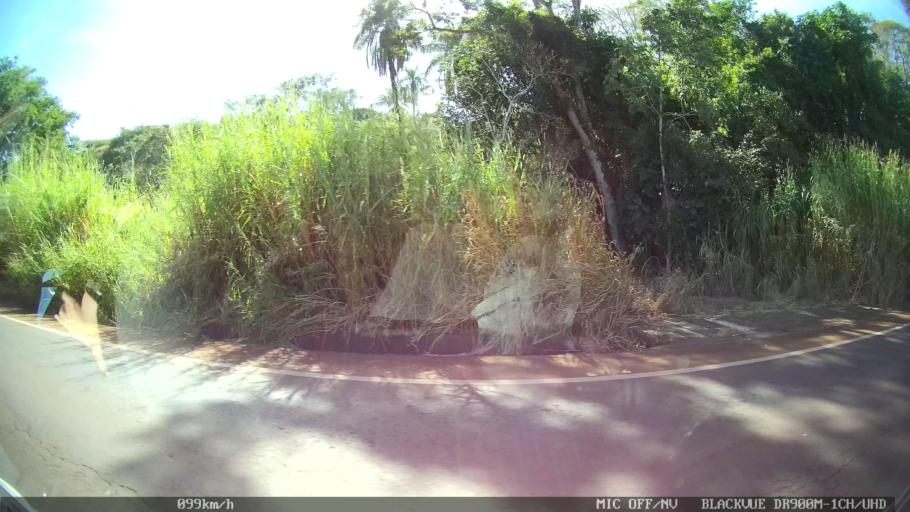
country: BR
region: Sao Paulo
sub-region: Sao Joaquim Da Barra
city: Sao Joaquim da Barra
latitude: -20.5535
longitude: -47.6709
